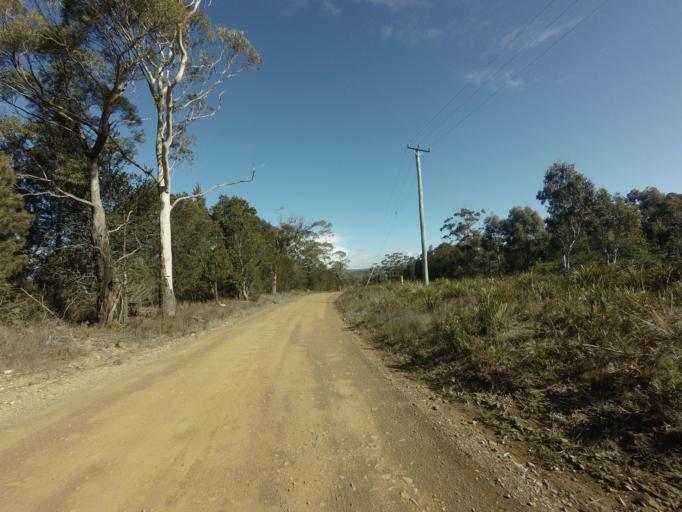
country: AU
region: Tasmania
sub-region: Sorell
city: Sorell
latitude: -42.3539
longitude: 147.9676
